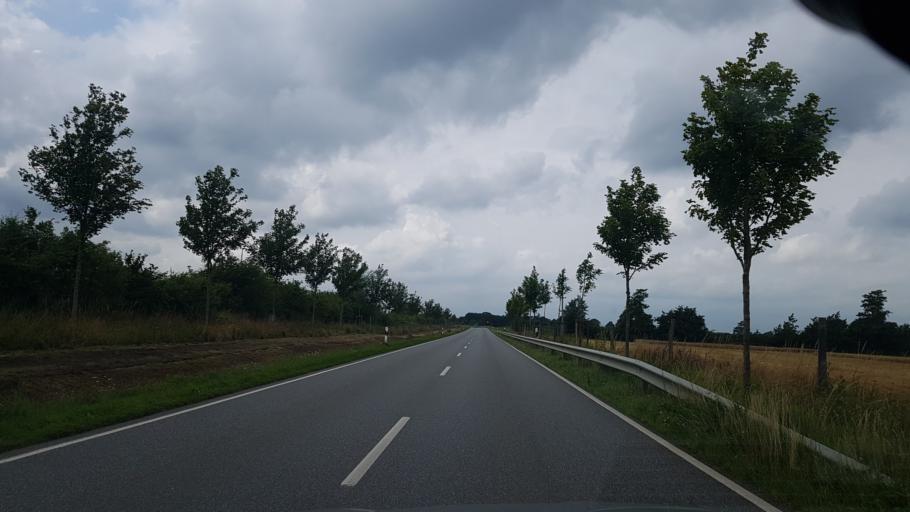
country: DE
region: Schleswig-Holstein
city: Boxlund
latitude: 54.8586
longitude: 9.1582
